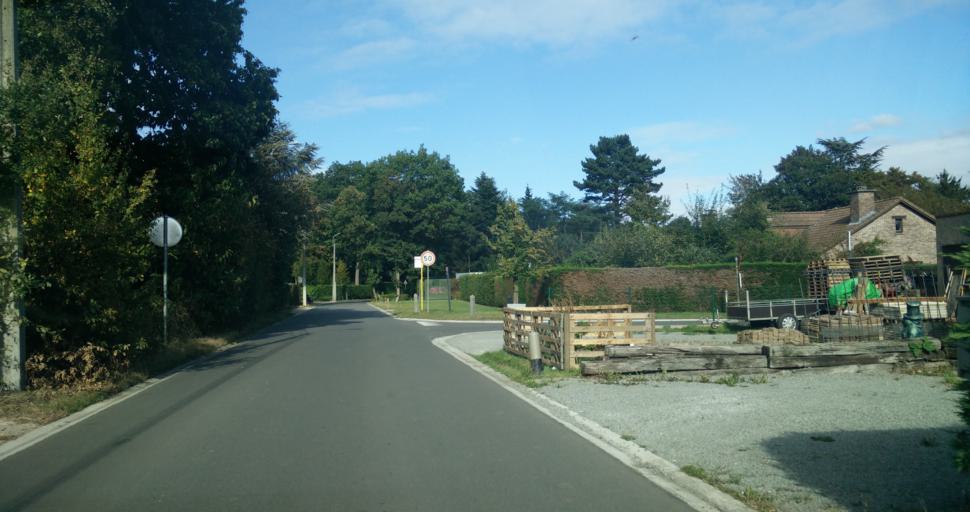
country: BE
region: Flanders
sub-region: Provincie Vlaams-Brabant
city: Halle
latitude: 50.7242
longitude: 4.2732
